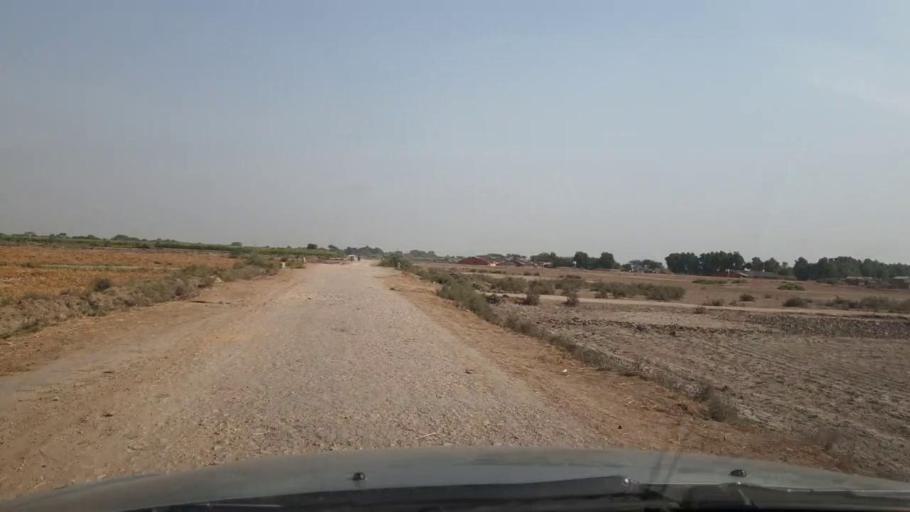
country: PK
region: Sindh
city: Bulri
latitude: 24.9142
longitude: 68.3632
